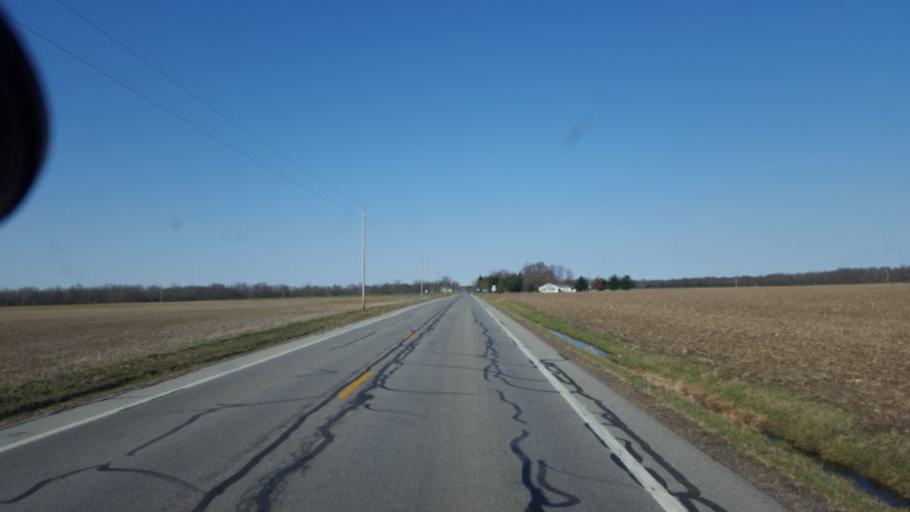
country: US
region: Ohio
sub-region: Morrow County
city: Cardington
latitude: 40.5865
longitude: -82.9580
